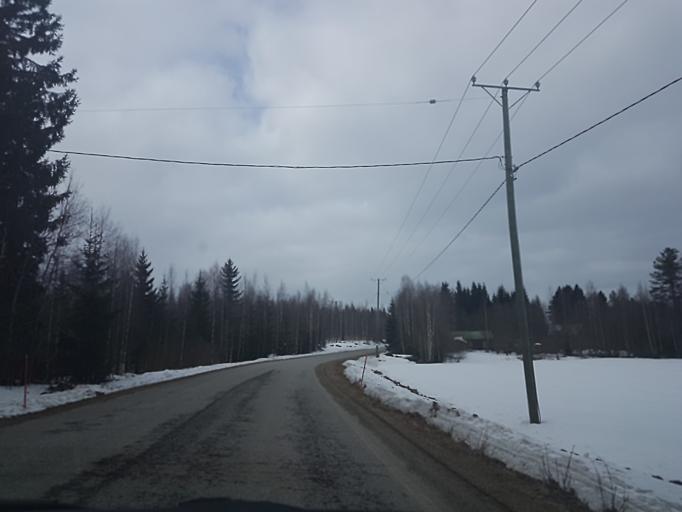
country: FI
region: Northern Savo
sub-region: Koillis-Savo
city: Kaavi
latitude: 63.0030
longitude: 28.6791
